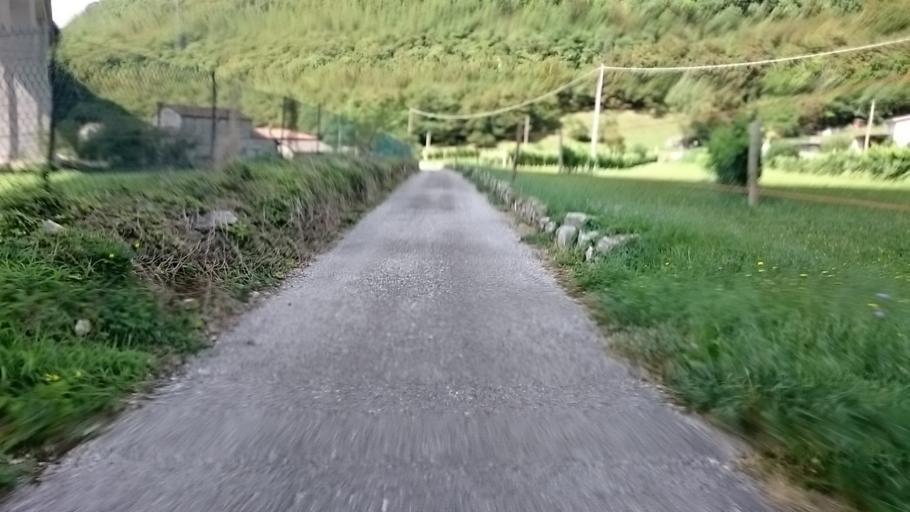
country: IT
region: Veneto
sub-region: Provincia di Treviso
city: Fregona
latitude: 46.0293
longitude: 12.3002
